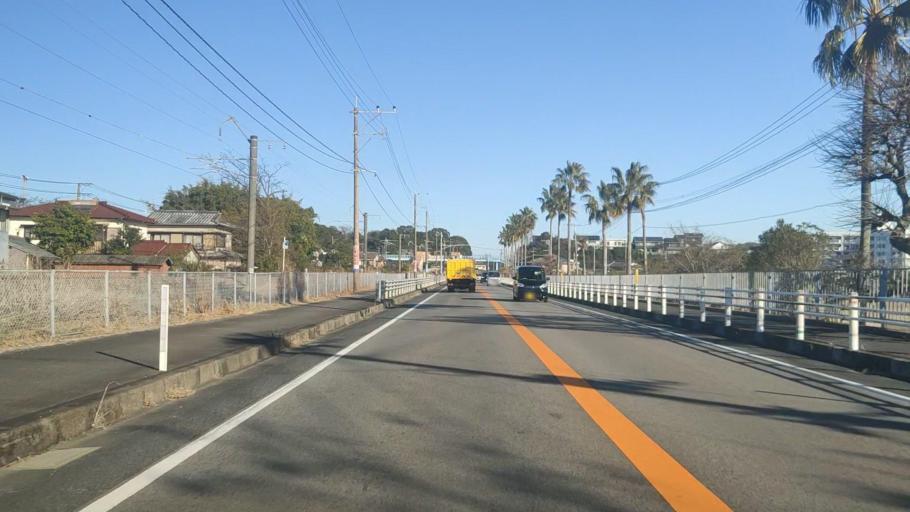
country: JP
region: Miyazaki
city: Nobeoka
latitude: 32.5145
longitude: 131.6824
